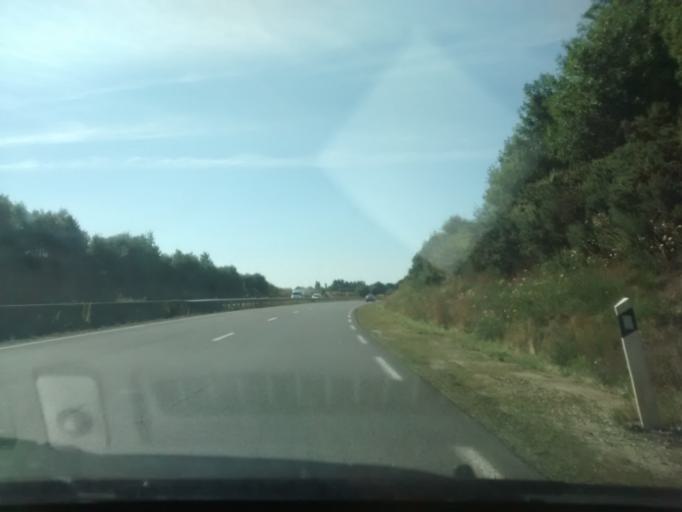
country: FR
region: Brittany
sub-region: Departement des Cotes-d'Armor
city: Begard
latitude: 48.6181
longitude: -3.3060
